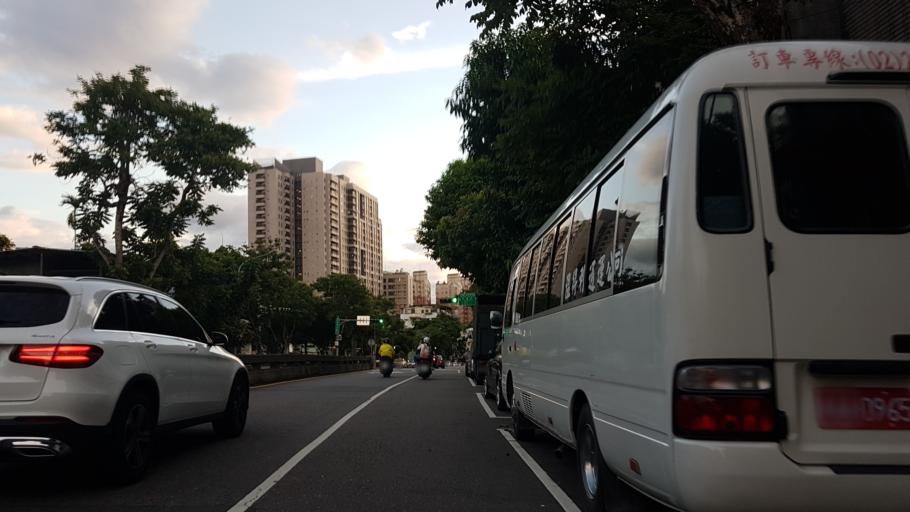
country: TW
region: Taipei
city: Taipei
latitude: 24.9901
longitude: 121.5654
